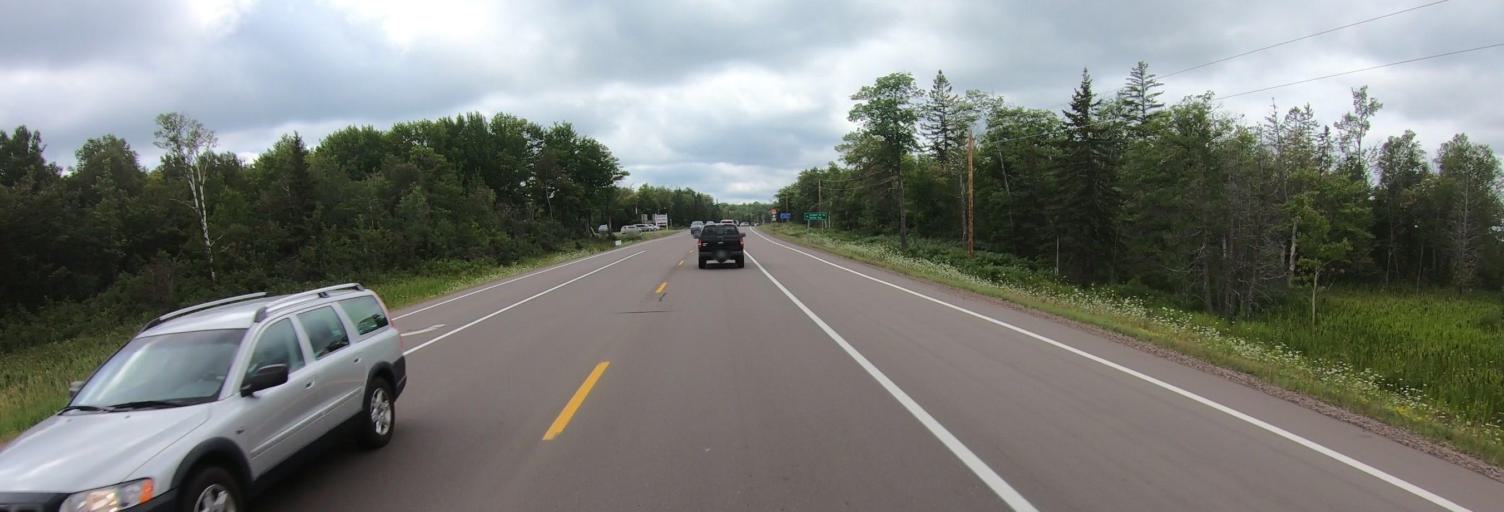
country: US
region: Michigan
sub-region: Houghton County
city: Dollar Bay
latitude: 47.1716
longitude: -88.5140
